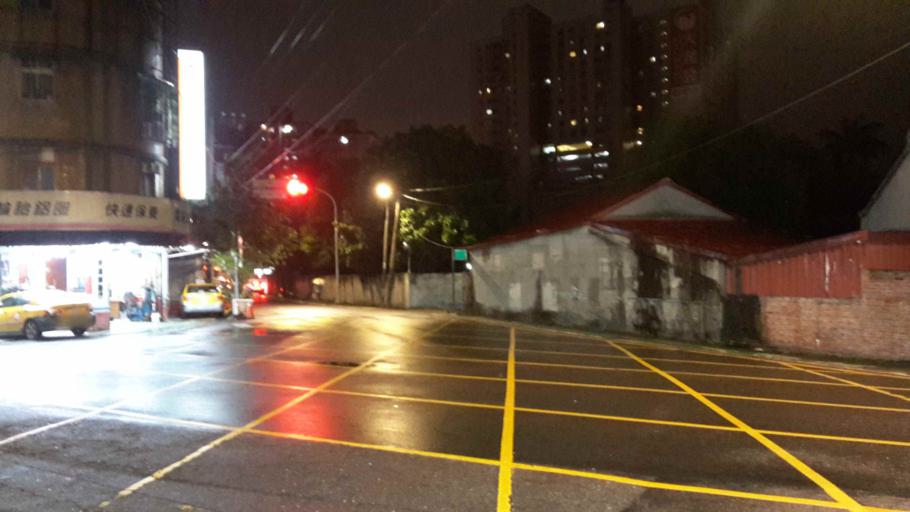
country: TW
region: Taipei
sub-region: Taipei
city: Banqiao
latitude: 25.0053
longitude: 121.4982
